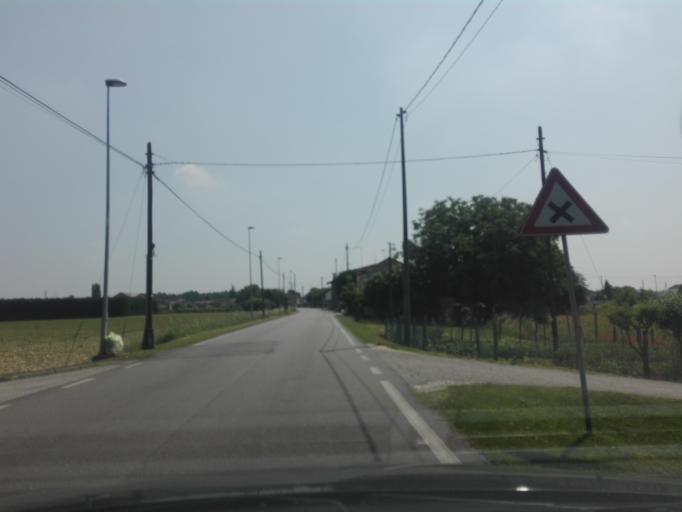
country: IT
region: Veneto
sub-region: Provincia di Rovigo
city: Lama Pezzoli
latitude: 45.0432
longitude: 11.9036
